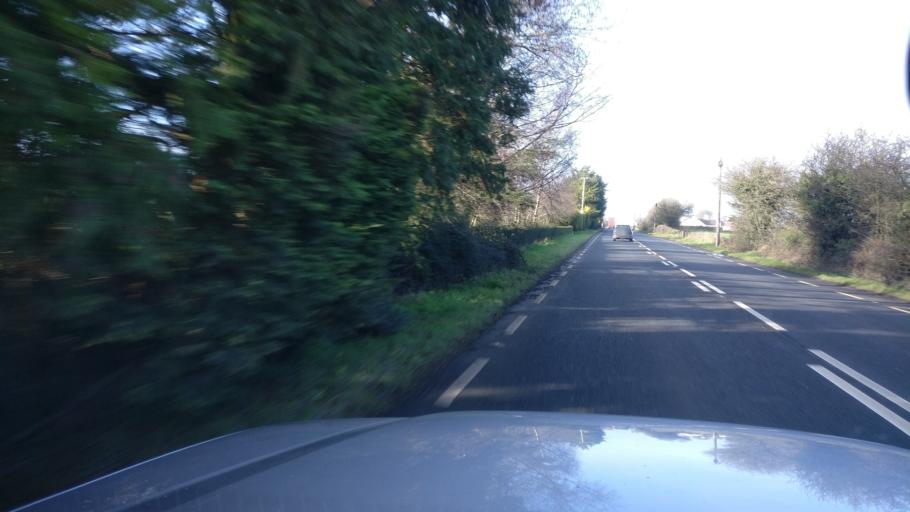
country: IE
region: Leinster
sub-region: Uibh Fhaili
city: Tullamore
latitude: 53.2072
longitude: -7.4361
